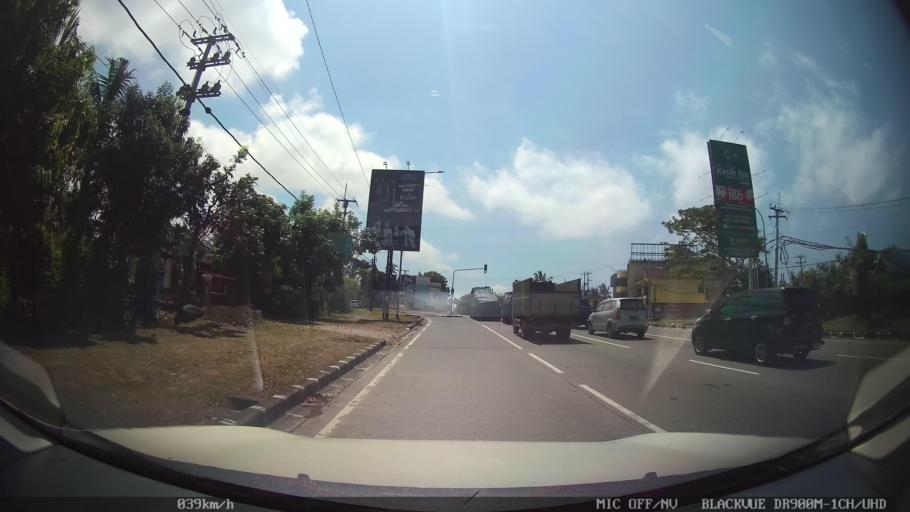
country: ID
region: Bali
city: Banjar Pasekan
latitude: -8.6085
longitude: 115.3148
